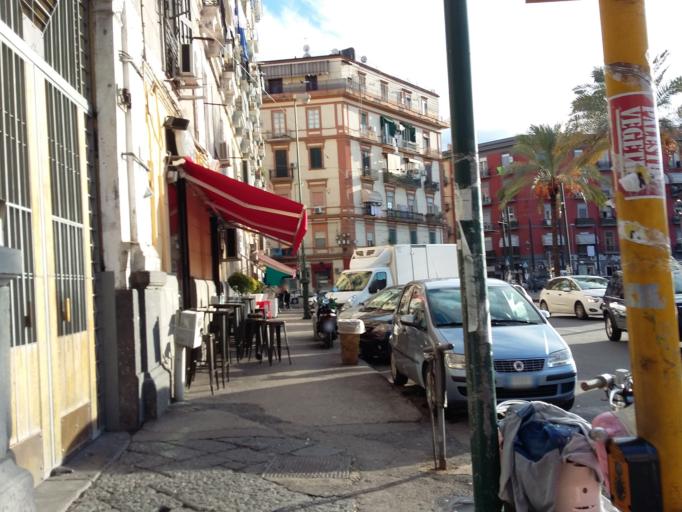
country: IT
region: Campania
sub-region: Provincia di Napoli
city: Napoli
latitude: 40.8586
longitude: 14.2746
